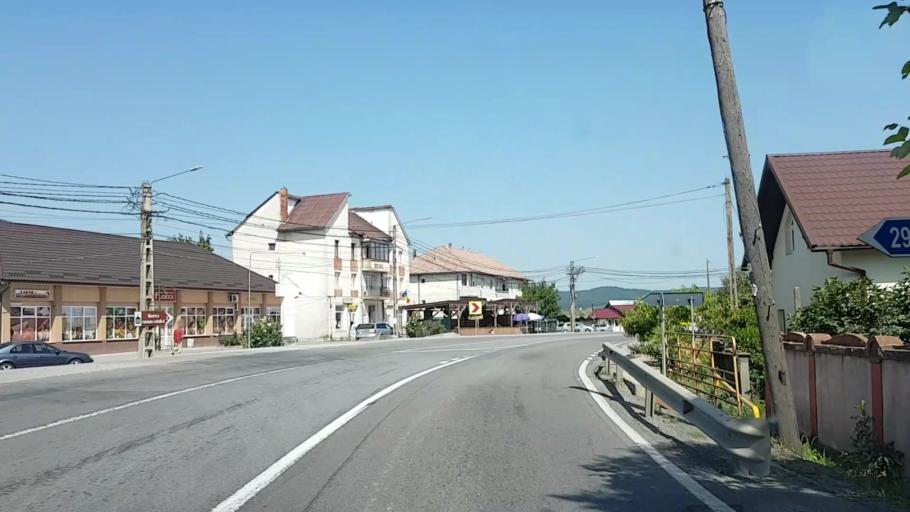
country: RO
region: Bistrita-Nasaud
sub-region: Comuna Uriu
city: Uriu
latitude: 47.2019
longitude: 24.0619
